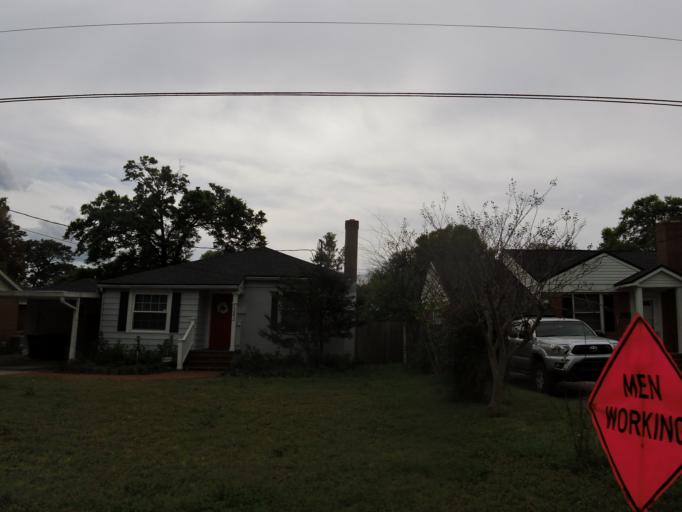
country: US
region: Florida
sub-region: Duval County
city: Jacksonville
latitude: 30.2792
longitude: -81.6558
